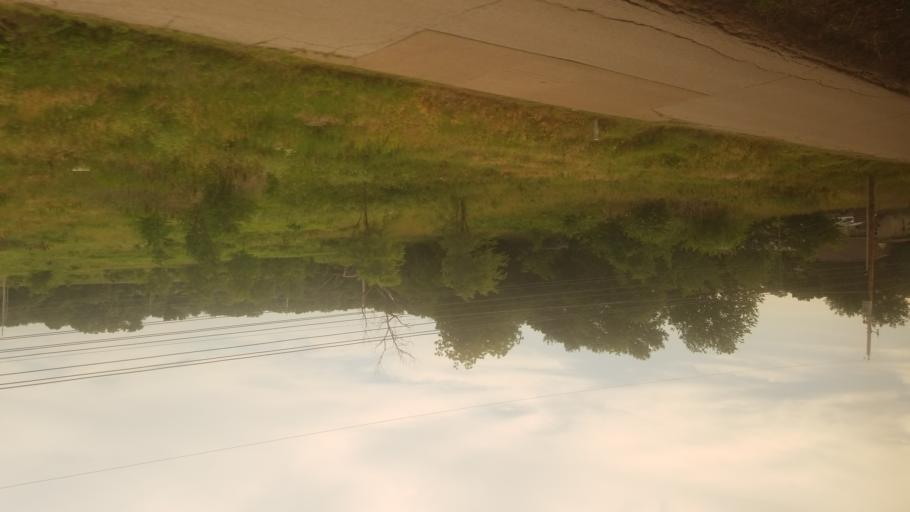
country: US
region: Kansas
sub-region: Shawnee County
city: Topeka
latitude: 39.0552
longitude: -95.6305
